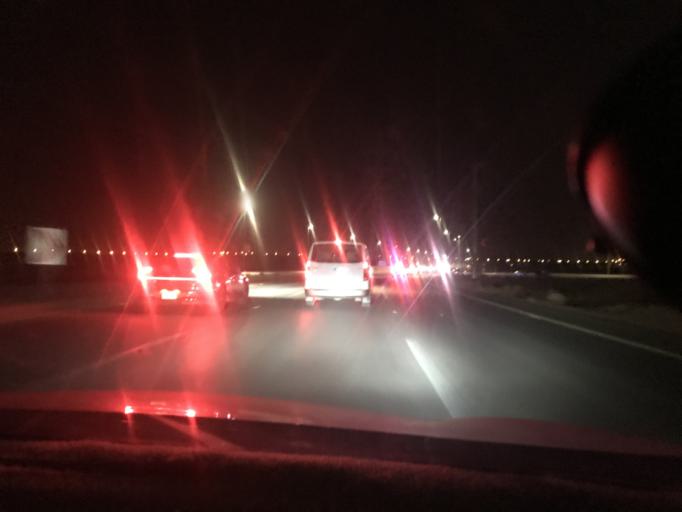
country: SA
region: Al-Qassim
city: Buraydah
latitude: 26.4072
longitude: 43.9618
